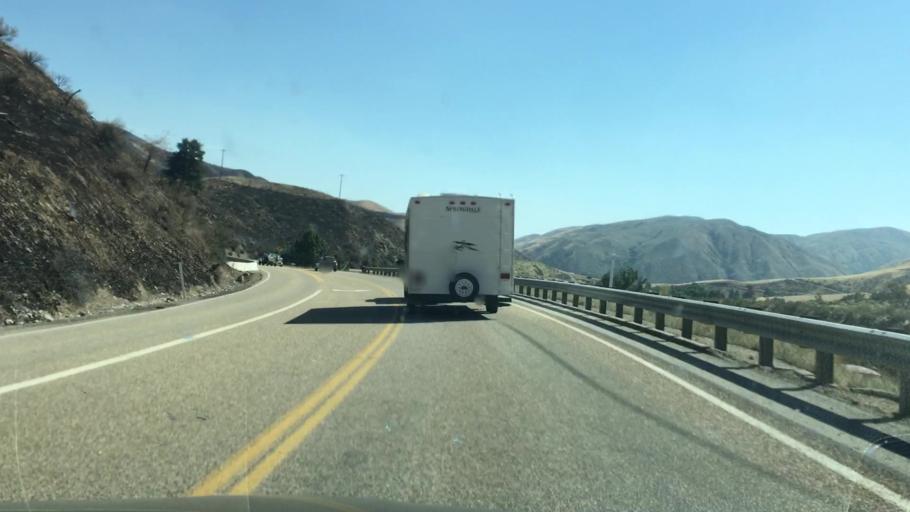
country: US
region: Idaho
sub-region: Gem County
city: Emmett
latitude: 44.0046
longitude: -116.1803
